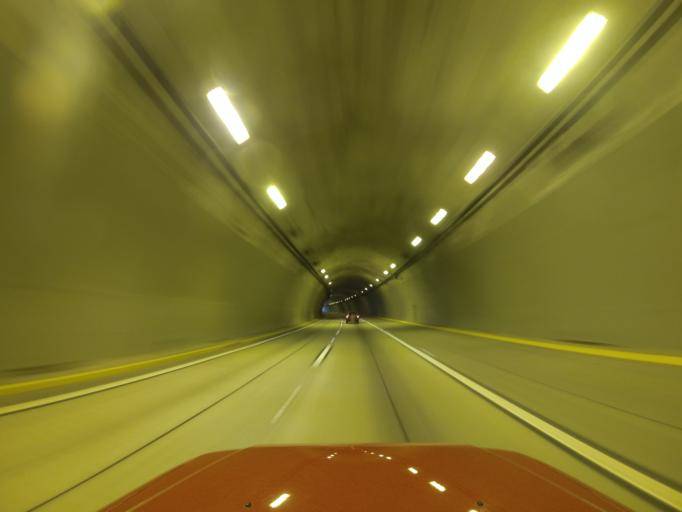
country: BR
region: Sao Paulo
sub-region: Jacarei
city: Jacarei
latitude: -23.3418
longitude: -45.9541
